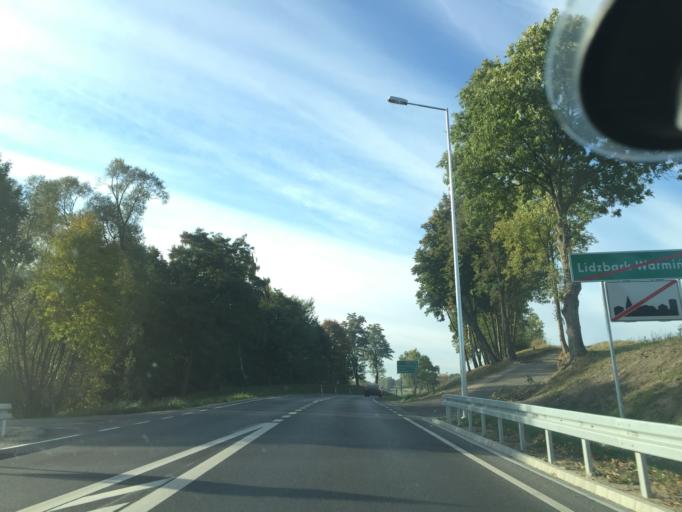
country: PL
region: Warmian-Masurian Voivodeship
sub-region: Powiat lidzbarski
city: Lidzbark Warminski
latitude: 54.1129
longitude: 20.5665
